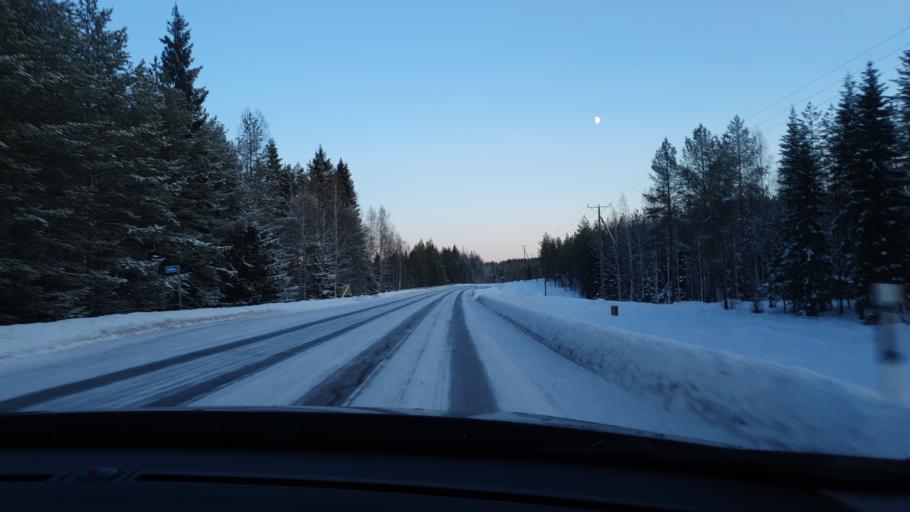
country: FI
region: Kainuu
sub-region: Kajaani
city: Sotkamo
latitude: 64.0907
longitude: 28.7365
